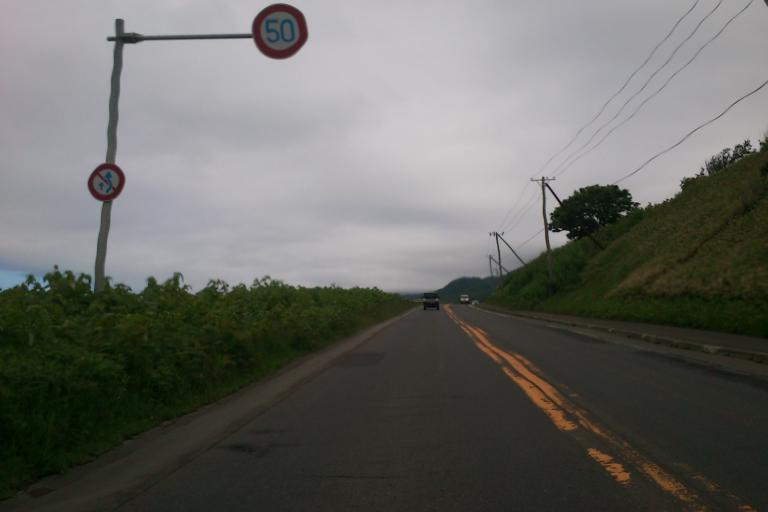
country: JP
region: Hokkaido
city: Ishikari
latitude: 43.4046
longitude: 141.4307
